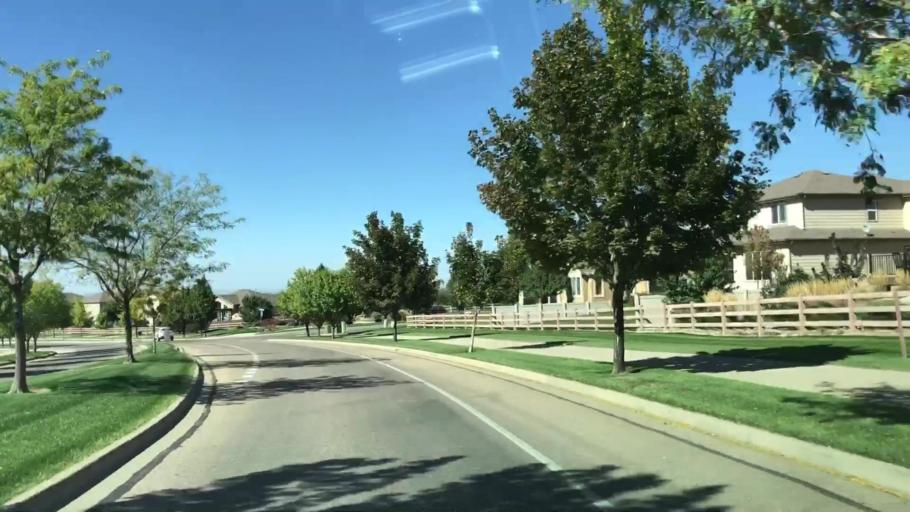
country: US
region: Colorado
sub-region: Weld County
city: Windsor
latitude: 40.4409
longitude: -104.9676
